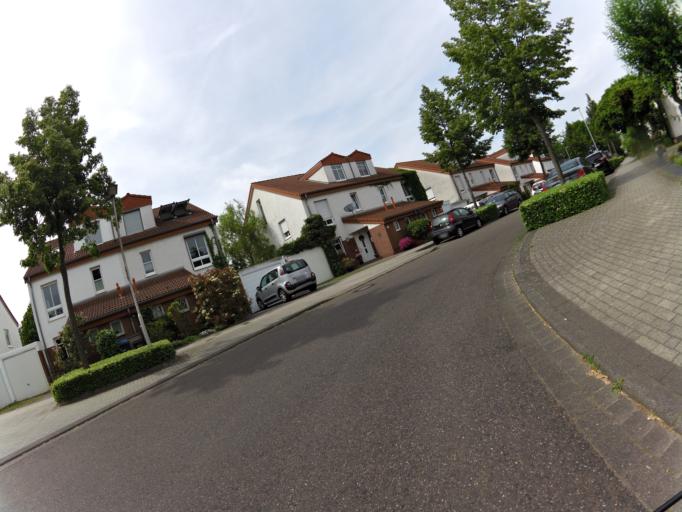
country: DE
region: North Rhine-Westphalia
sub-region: Regierungsbezirk Koln
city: Wurselen
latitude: 50.8270
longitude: 6.1320
